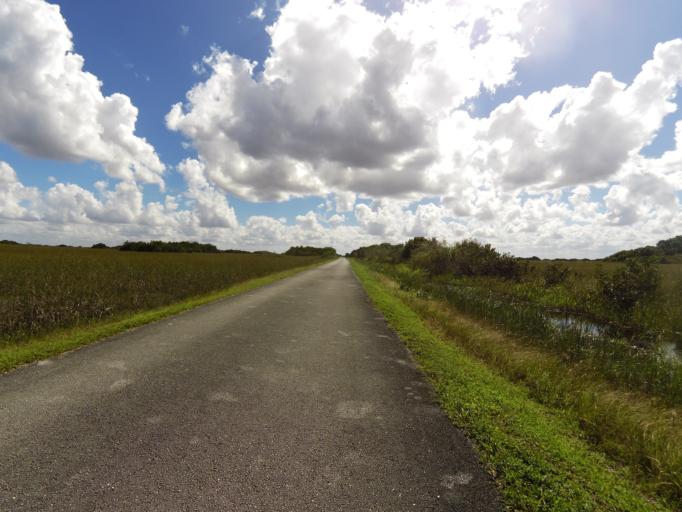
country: US
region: Florida
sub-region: Miami-Dade County
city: The Hammocks
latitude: 25.6904
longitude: -80.7669
